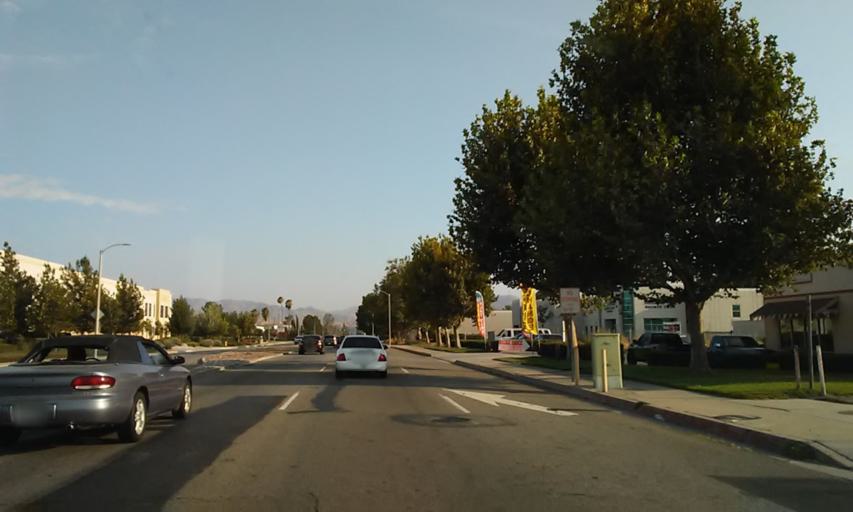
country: US
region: California
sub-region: San Bernardino County
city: San Bernardino
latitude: 34.0911
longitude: -117.2788
